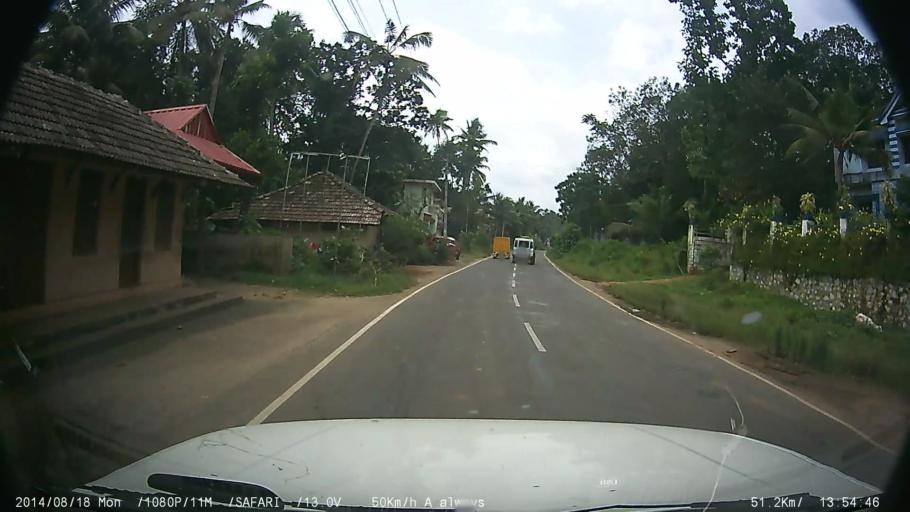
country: IN
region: Kerala
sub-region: Kottayam
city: Palackattumala
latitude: 9.7419
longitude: 76.5599
